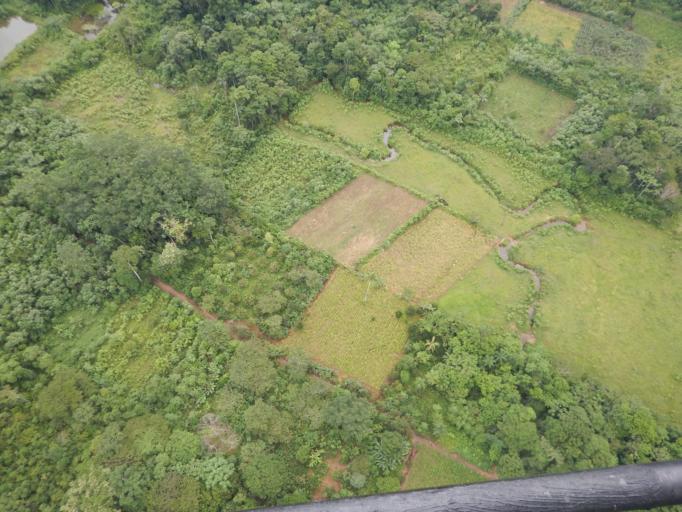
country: BO
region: Cochabamba
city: Chimore
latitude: -17.2582
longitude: -64.6574
